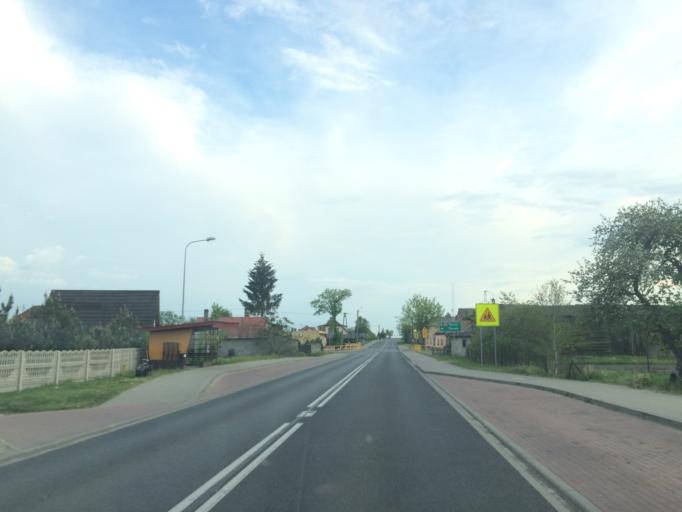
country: PL
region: Kujawsko-Pomorskie
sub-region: Powiat brodnicki
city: Brzozie
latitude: 53.3437
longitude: 19.5651
